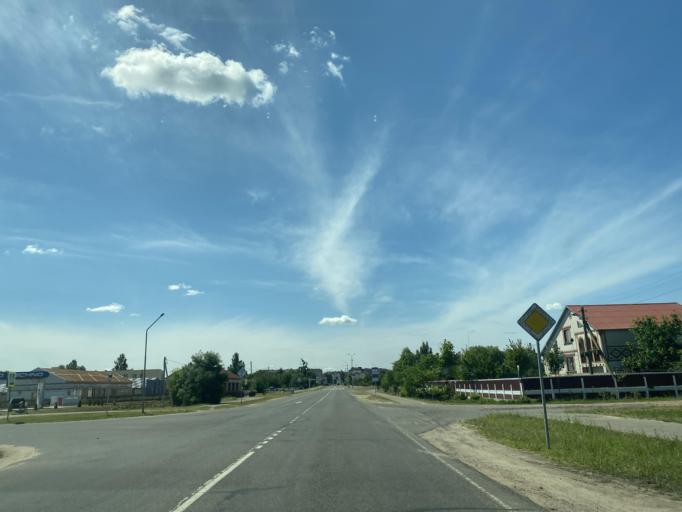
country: BY
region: Brest
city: Ivanava
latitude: 52.1559
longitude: 25.5444
